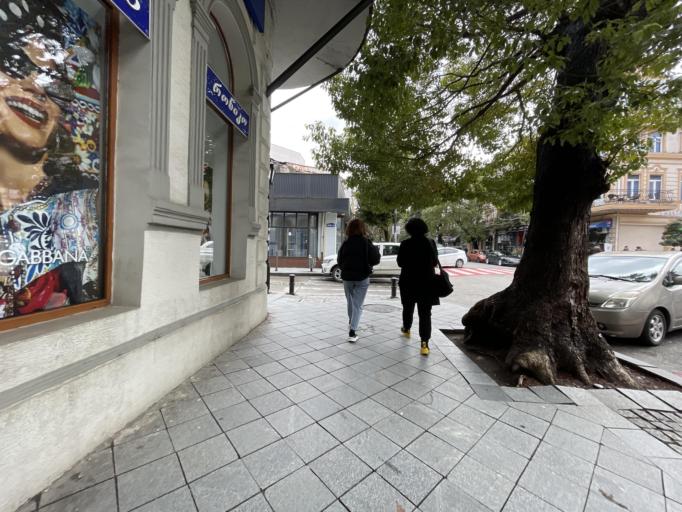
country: GE
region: Ajaria
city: Batumi
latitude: 41.6477
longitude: 41.6403
